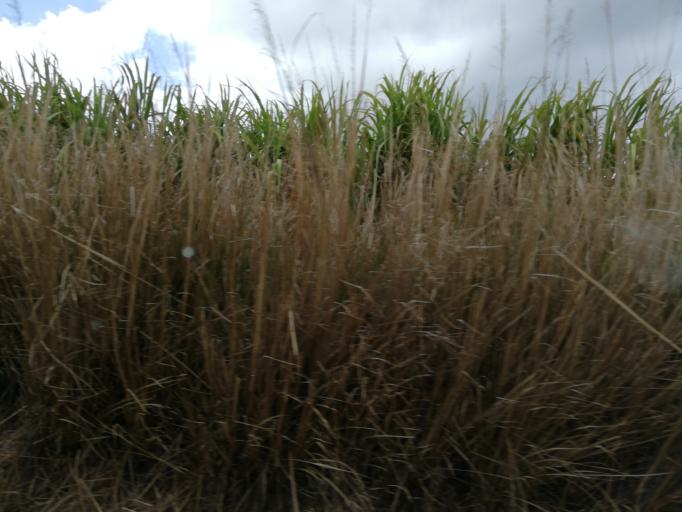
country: MU
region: Pamplemousses
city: Arsenal
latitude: -20.0932
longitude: 57.5430
